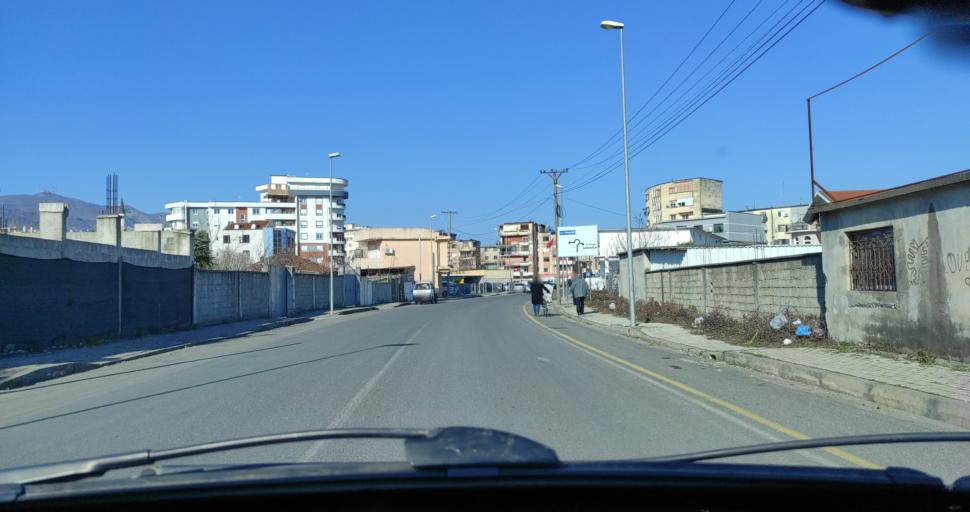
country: AL
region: Shkoder
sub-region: Rrethi i Shkodres
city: Shkoder
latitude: 42.0572
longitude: 19.5055
